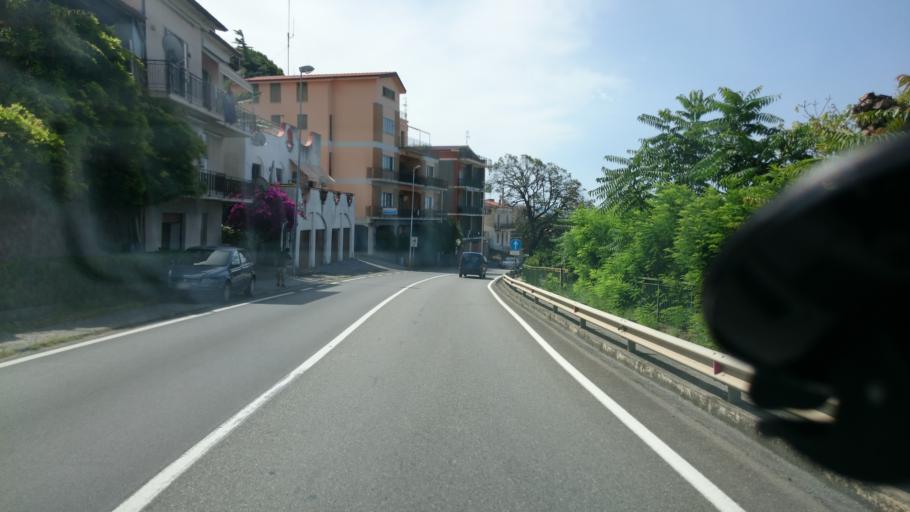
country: IT
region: Calabria
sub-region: Provincia di Cosenza
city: Scalea
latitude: 39.8182
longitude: 15.7869
